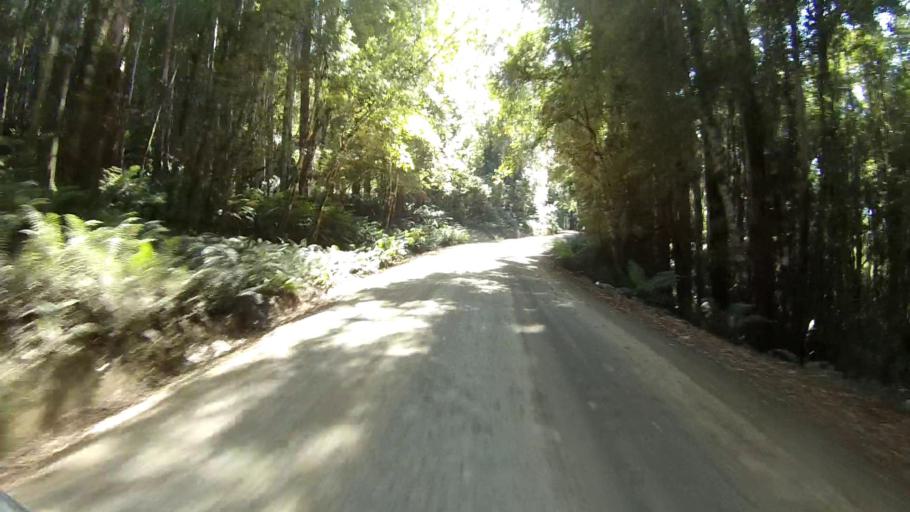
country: AU
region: Tasmania
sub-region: Derwent Valley
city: New Norfolk
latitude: -42.6776
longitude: 146.7014
